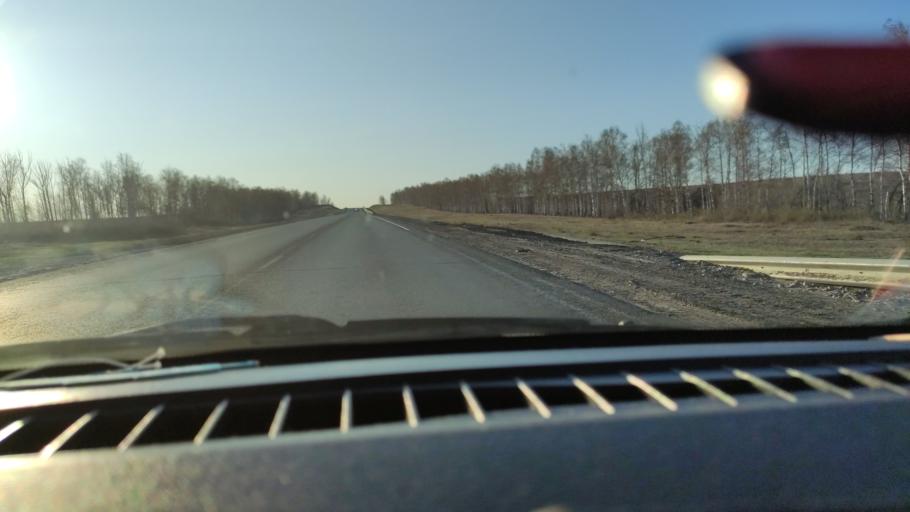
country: RU
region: Saratov
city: Shikhany
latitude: 52.1249
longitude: 47.2476
